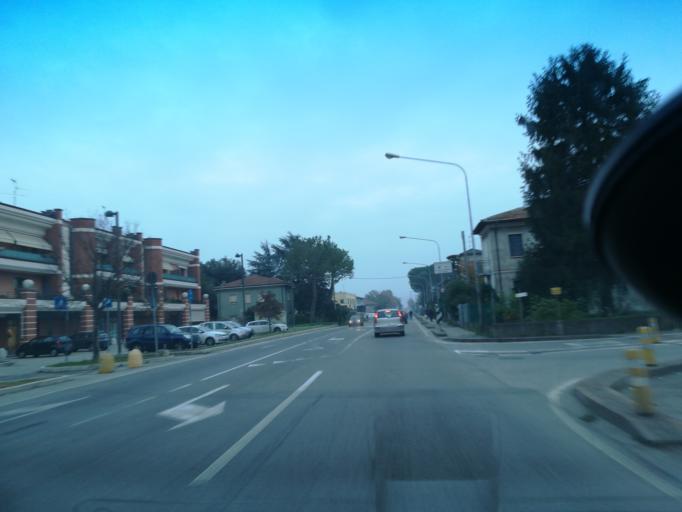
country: IT
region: Emilia-Romagna
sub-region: Provincia di Ravenna
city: Castel Bolognese
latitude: 44.3188
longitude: 11.8018
